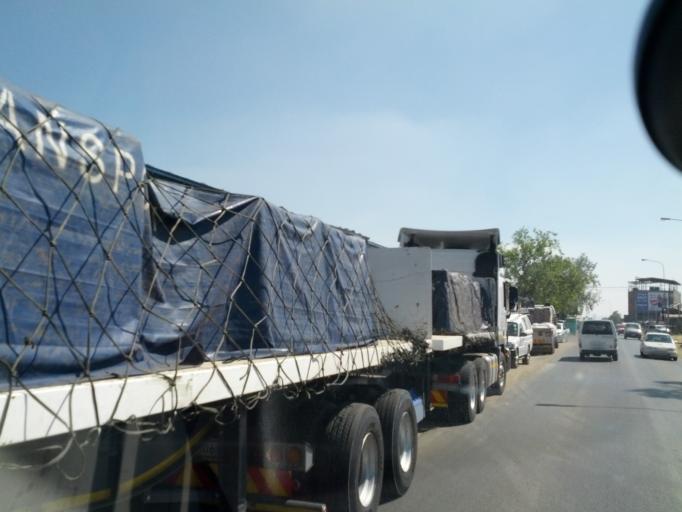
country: LS
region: Berea
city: Teyateyaneng
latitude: -29.1505
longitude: 27.7467
